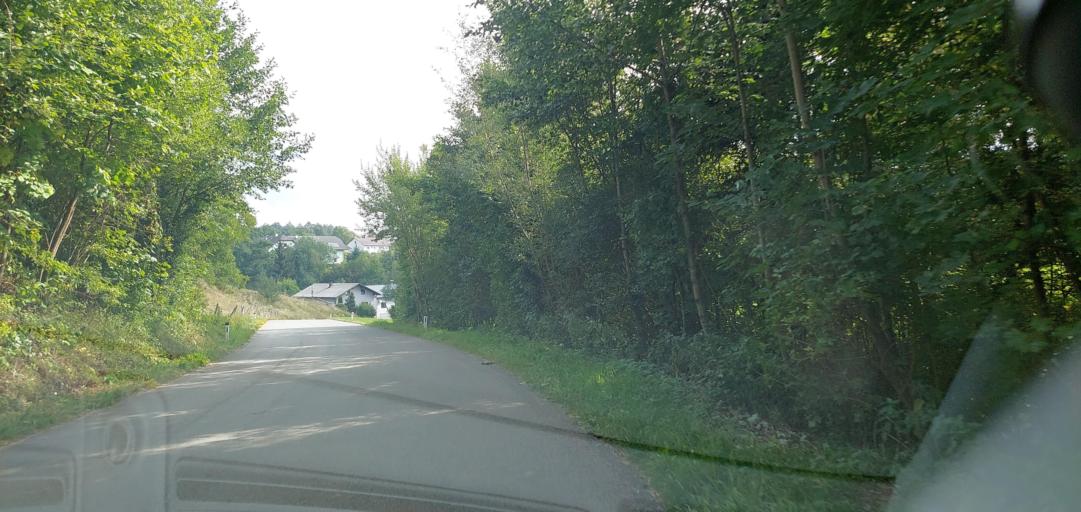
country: AT
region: Upper Austria
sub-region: Politischer Bezirk Urfahr-Umgebung
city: Feldkirchen an der Donau
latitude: 48.3402
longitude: 13.9664
